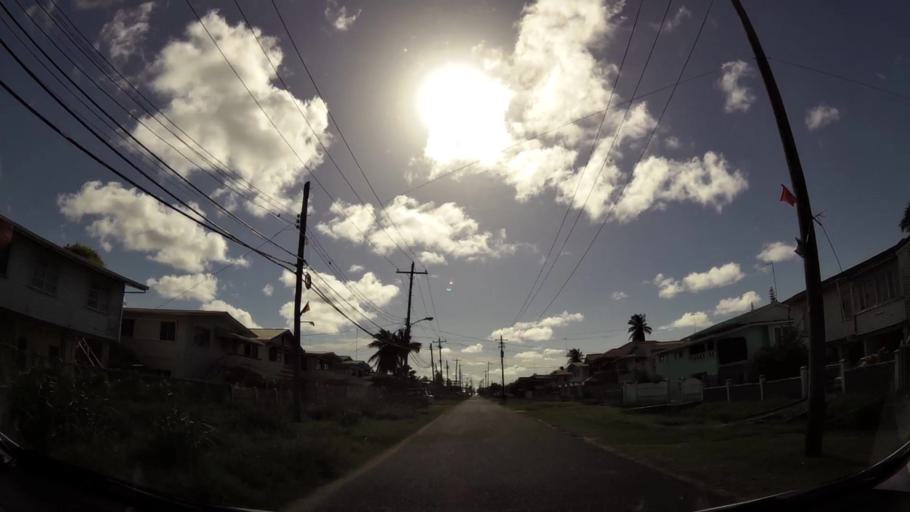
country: GY
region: Demerara-Mahaica
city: Georgetown
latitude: 6.8141
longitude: -58.1299
